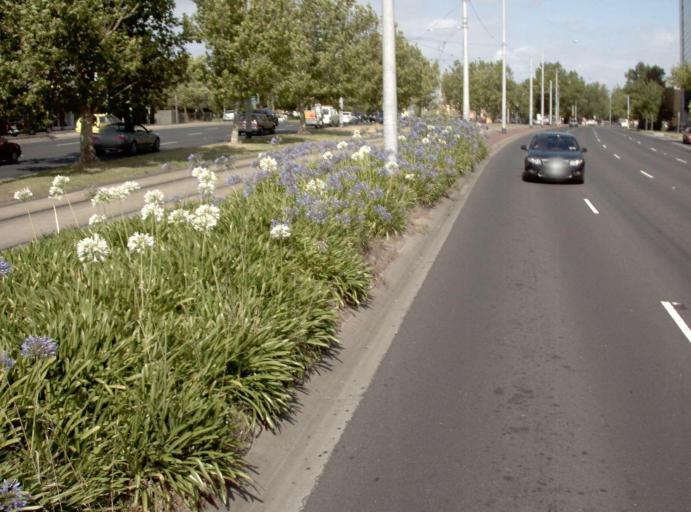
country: AU
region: Victoria
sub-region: Stonnington
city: Malvern East
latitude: -37.8756
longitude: 145.0425
